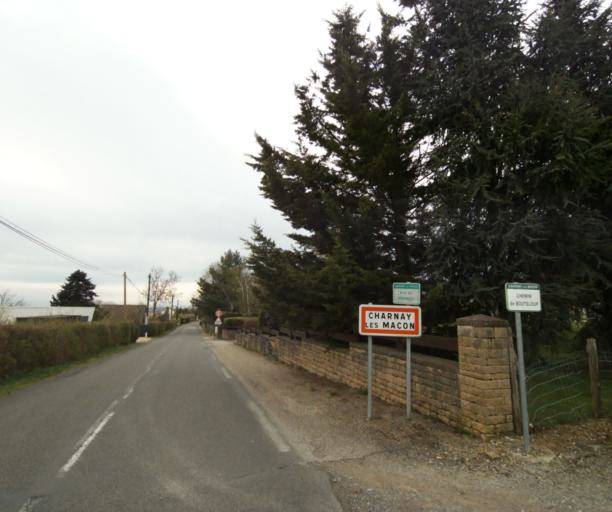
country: FR
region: Bourgogne
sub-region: Departement de Saone-et-Loire
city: Charnay-les-Macon
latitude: 46.3240
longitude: 4.7869
